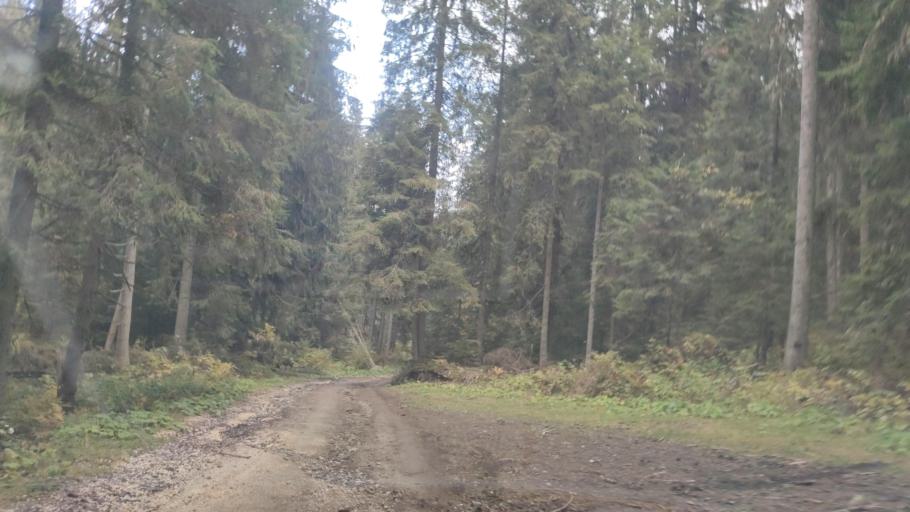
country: RO
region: Harghita
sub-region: Comuna Madaras
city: Madaras
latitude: 46.4719
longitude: 25.6381
